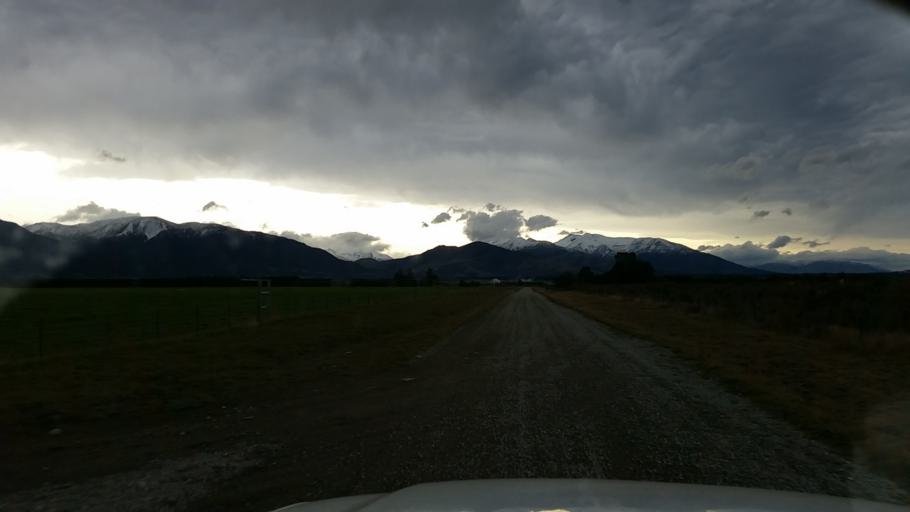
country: NZ
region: Canterbury
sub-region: Ashburton District
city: Methven
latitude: -43.7040
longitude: 171.4600
